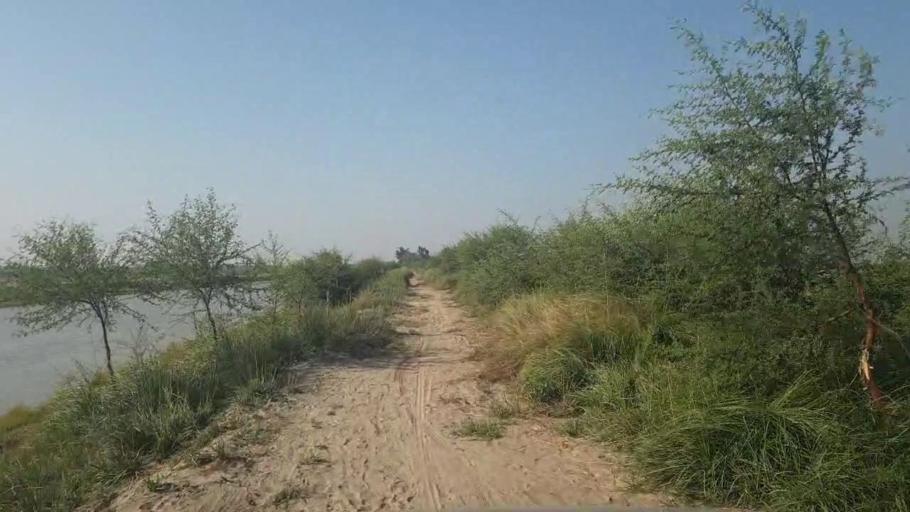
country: PK
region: Sindh
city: Badin
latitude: 24.6966
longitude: 68.8743
